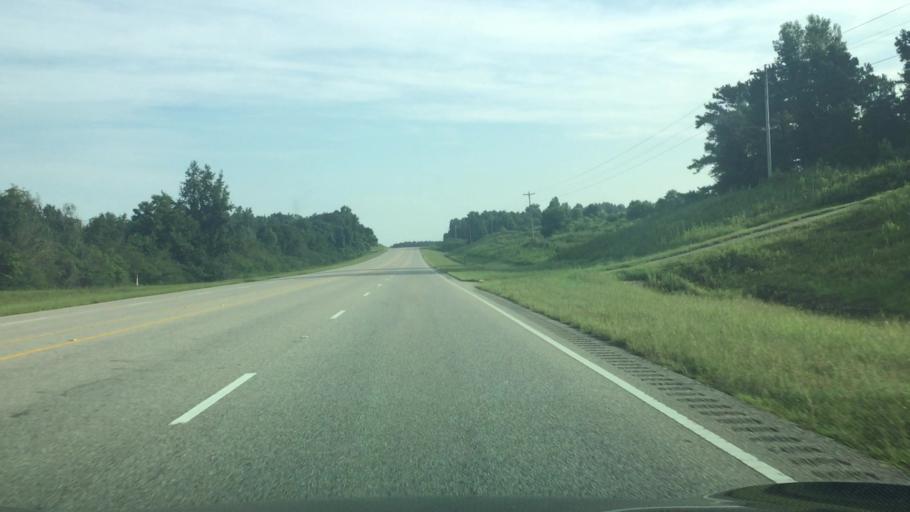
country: US
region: Alabama
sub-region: Covington County
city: Andalusia
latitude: 31.4292
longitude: -86.6116
